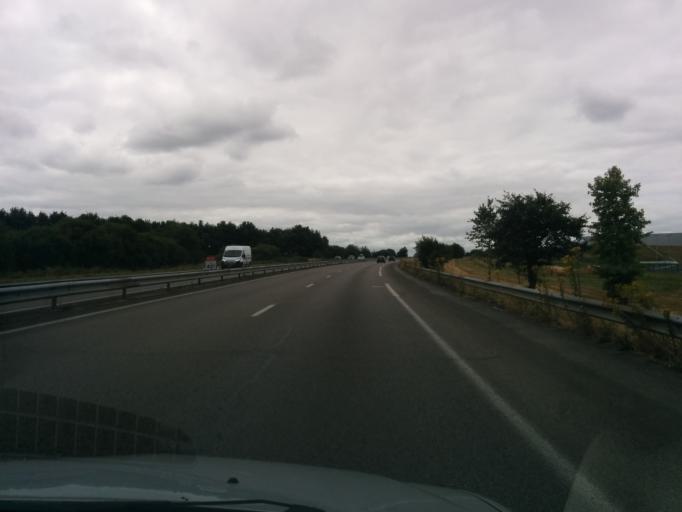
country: FR
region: Pays de la Loire
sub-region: Departement de la Loire-Atlantique
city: Heric
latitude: 47.3733
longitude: -1.6442
